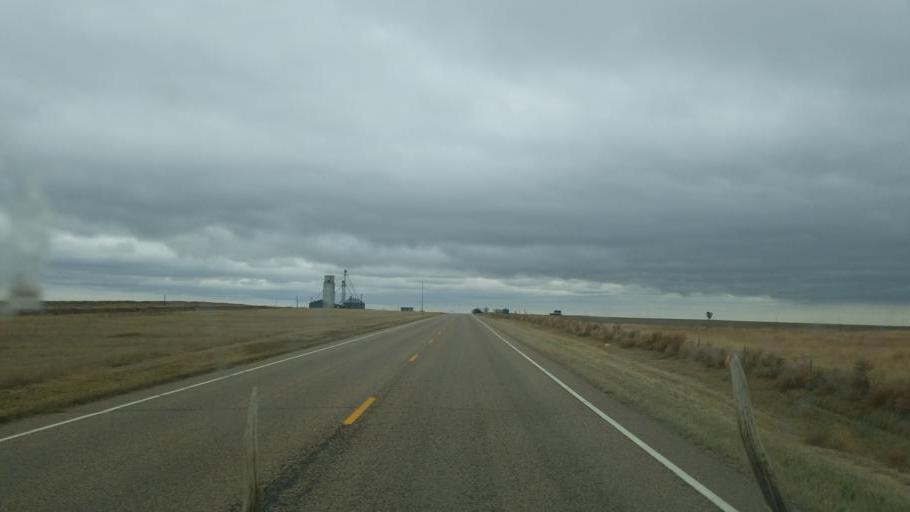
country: US
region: Colorado
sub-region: Cheyenne County
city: Cheyenne Wells
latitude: 38.8160
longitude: -102.5477
